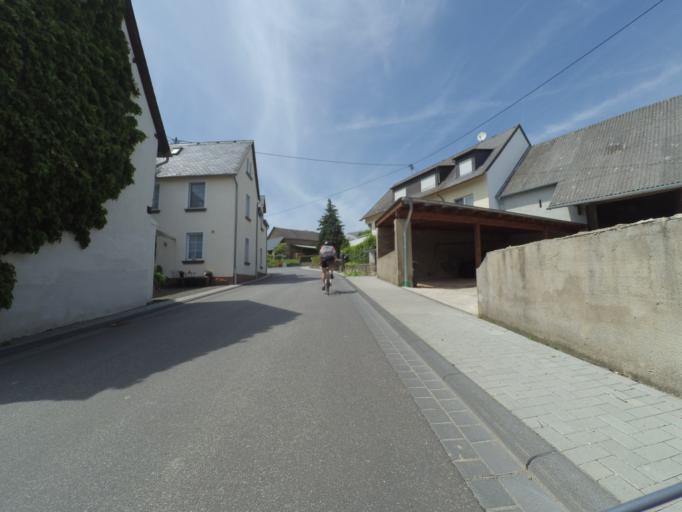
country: DE
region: Rheinland-Pfalz
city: Montenich
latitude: 50.2218
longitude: 7.3011
